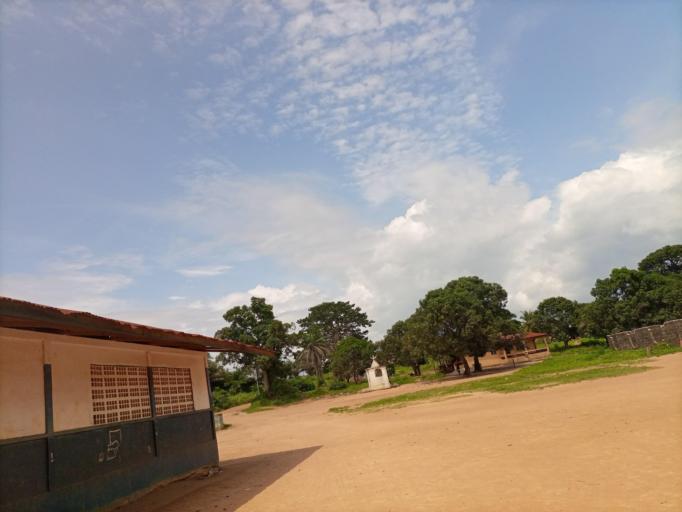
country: SL
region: Western Area
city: Freetown
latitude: 8.5253
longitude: -13.1468
